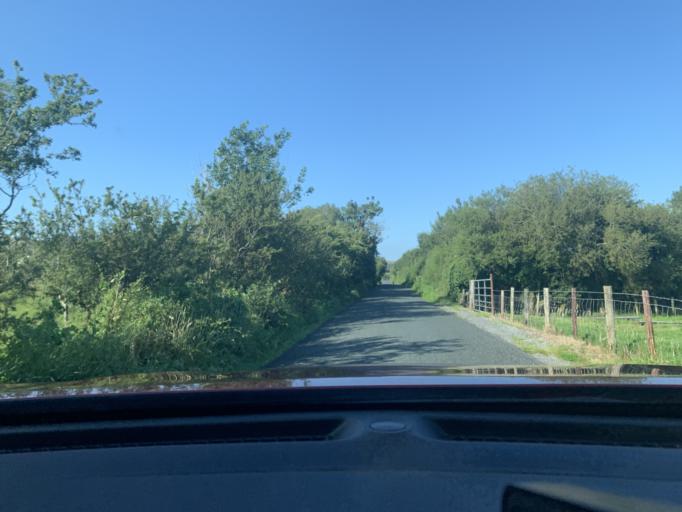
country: IE
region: Connaught
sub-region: Sligo
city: Tobercurry
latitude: 54.1075
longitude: -8.7711
